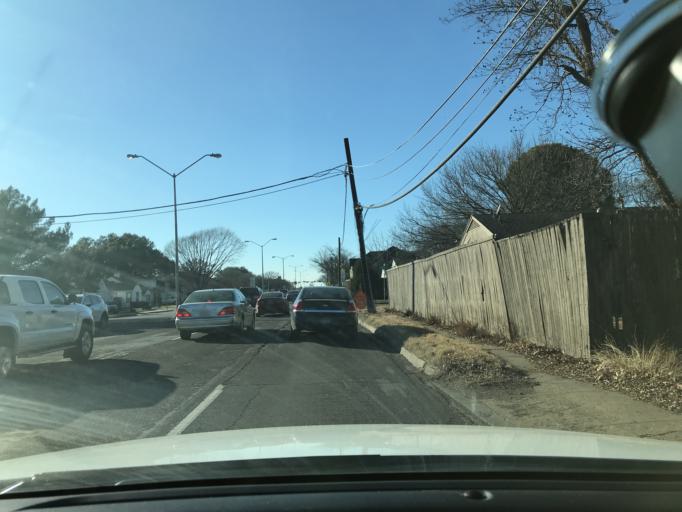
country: US
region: Texas
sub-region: Dallas County
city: Highland Park
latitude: 32.8366
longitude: -96.7638
